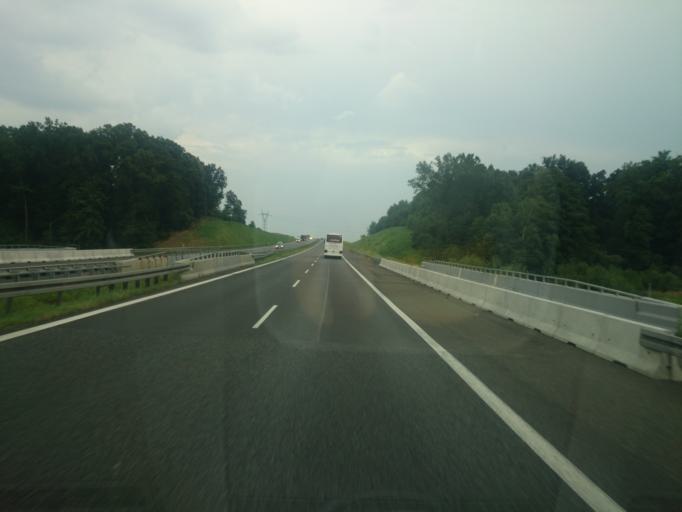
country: PL
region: Silesian Voivodeship
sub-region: Powiat gliwicki
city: Rudziniec
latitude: 50.4073
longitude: 18.4158
